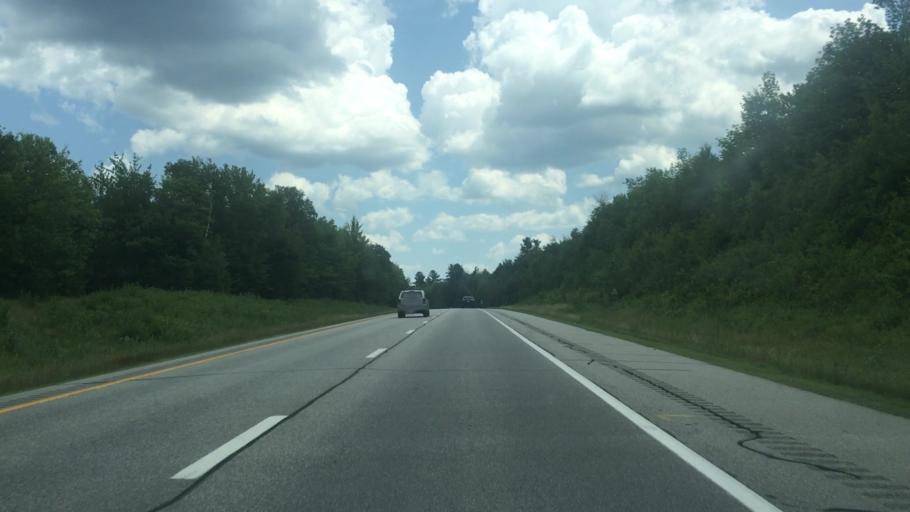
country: US
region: New Hampshire
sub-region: Merrimack County
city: New London
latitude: 43.3996
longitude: -72.0148
